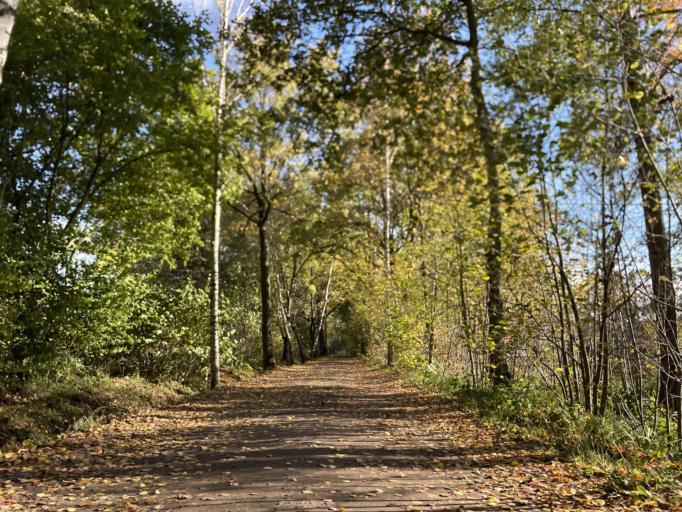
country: DE
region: Lower Saxony
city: Lueneburg
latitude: 53.2246
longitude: 10.4139
